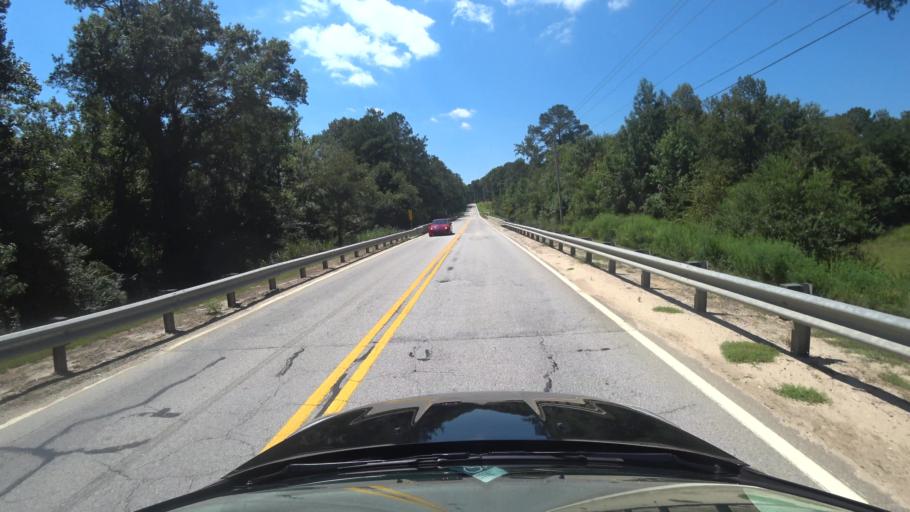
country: US
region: Georgia
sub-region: Newton County
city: Oxford
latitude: 33.6423
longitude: -83.7971
